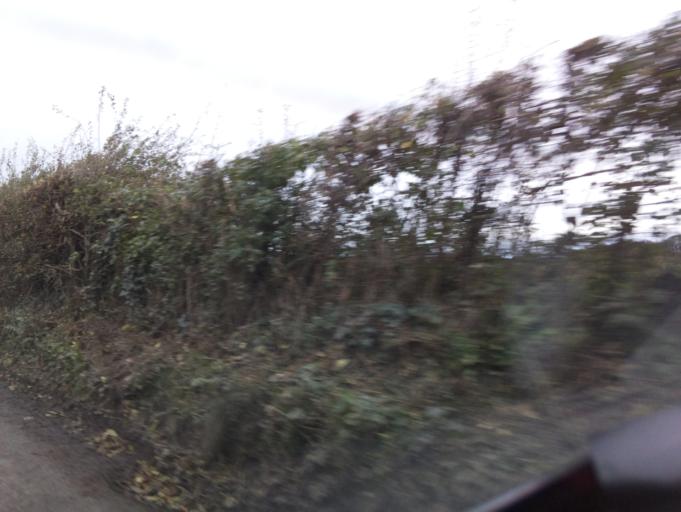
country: GB
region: England
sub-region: Somerset
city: South Petherton
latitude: 50.9330
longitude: -2.8261
